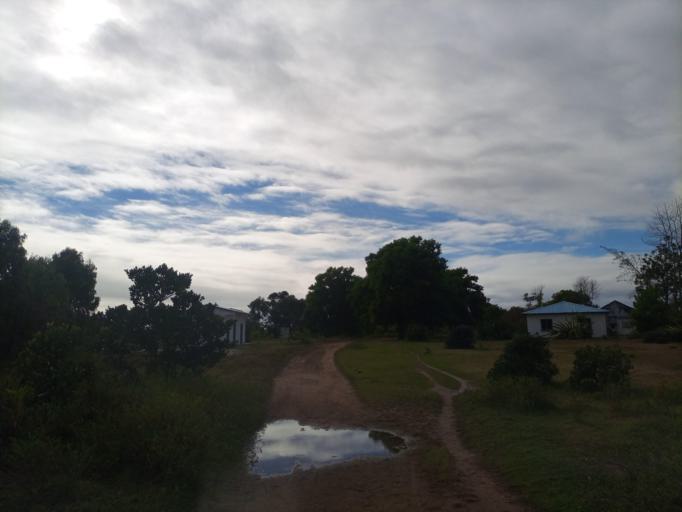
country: MG
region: Anosy
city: Fort Dauphin
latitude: -24.7795
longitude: 47.1815
